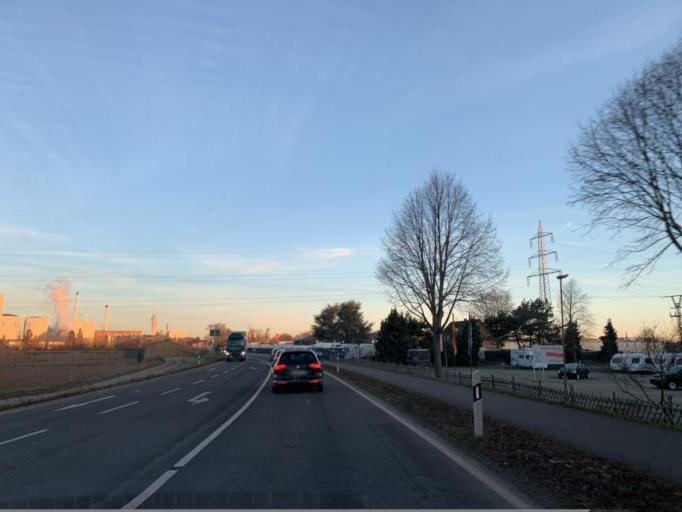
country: DE
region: North Rhine-Westphalia
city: Julich
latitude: 50.9082
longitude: 6.3795
